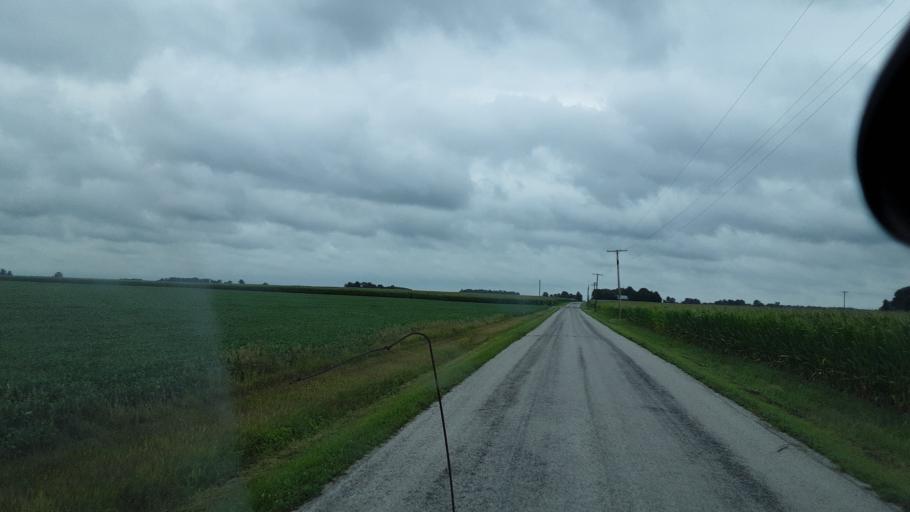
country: US
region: Indiana
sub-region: Wells County
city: Bluffton
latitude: 40.8033
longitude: -85.0714
